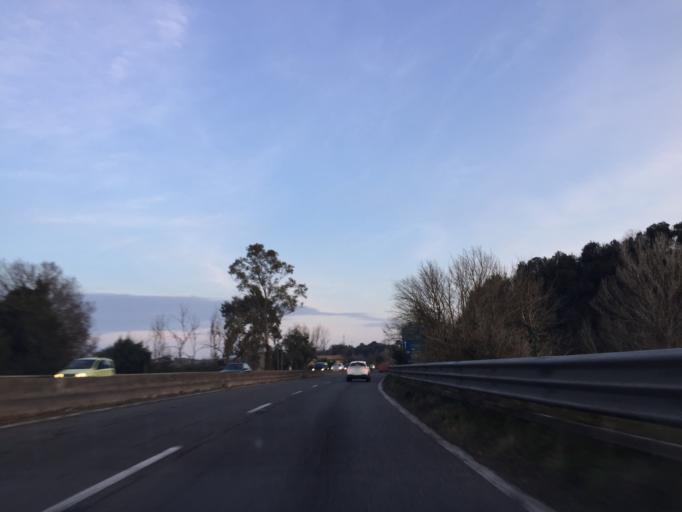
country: IT
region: Latium
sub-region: Citta metropolitana di Roma Capitale
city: Monte Caminetto
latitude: 41.9940
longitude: 12.4666
